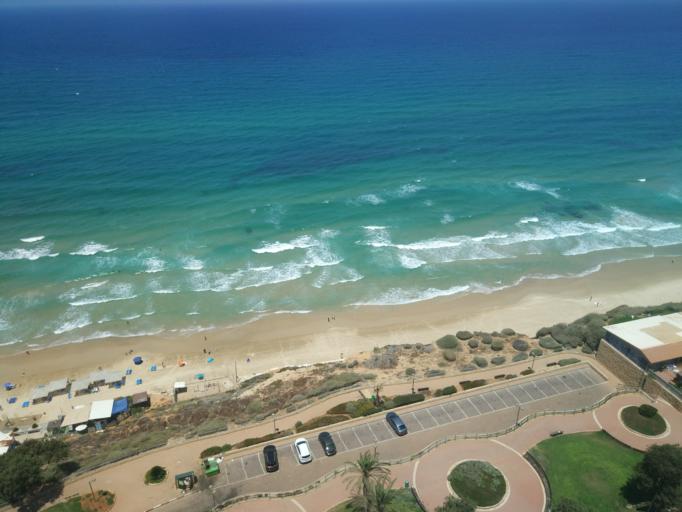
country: IL
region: Central District
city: Netanya
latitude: 32.3386
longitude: 34.8525
